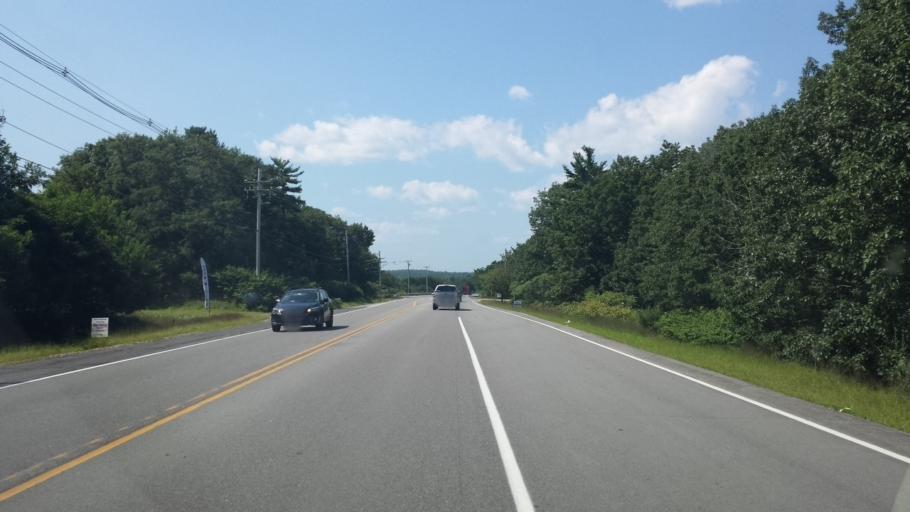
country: US
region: Maine
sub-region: York County
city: Biddeford
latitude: 43.4708
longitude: -70.4875
